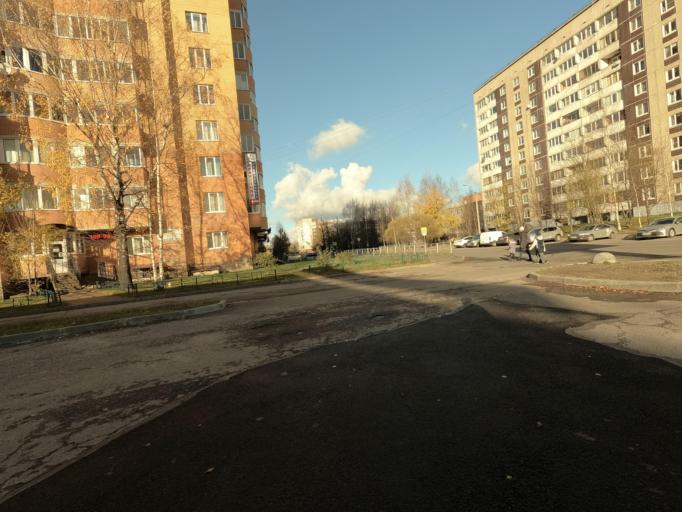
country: RU
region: Leningrad
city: Vsevolozhsk
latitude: 60.0286
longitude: 30.6296
